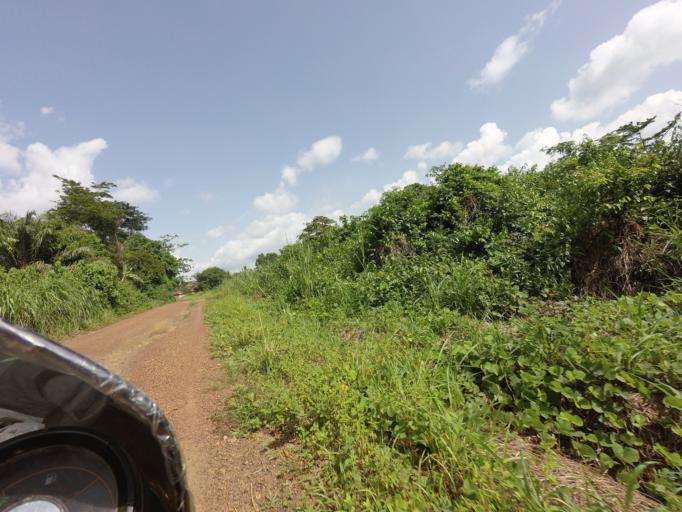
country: SL
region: Eastern Province
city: Daru
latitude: 8.0050
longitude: -10.8725
